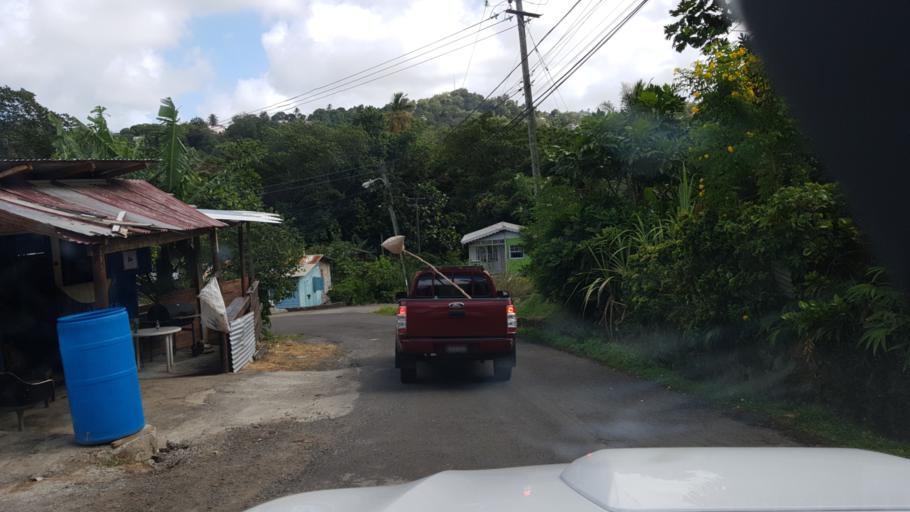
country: LC
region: Castries Quarter
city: Bisee
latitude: 14.0139
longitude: -60.9609
